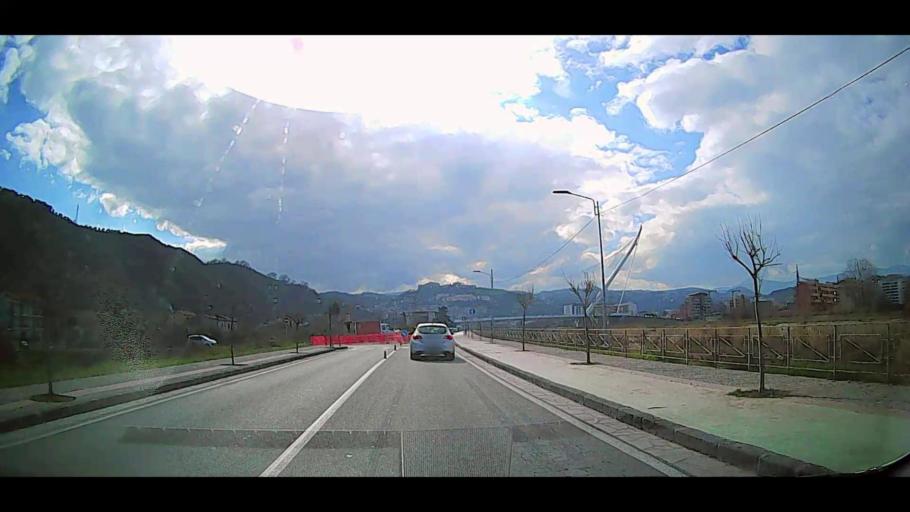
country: IT
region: Calabria
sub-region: Provincia di Cosenza
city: Cosenza
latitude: 39.3022
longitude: 16.2628
